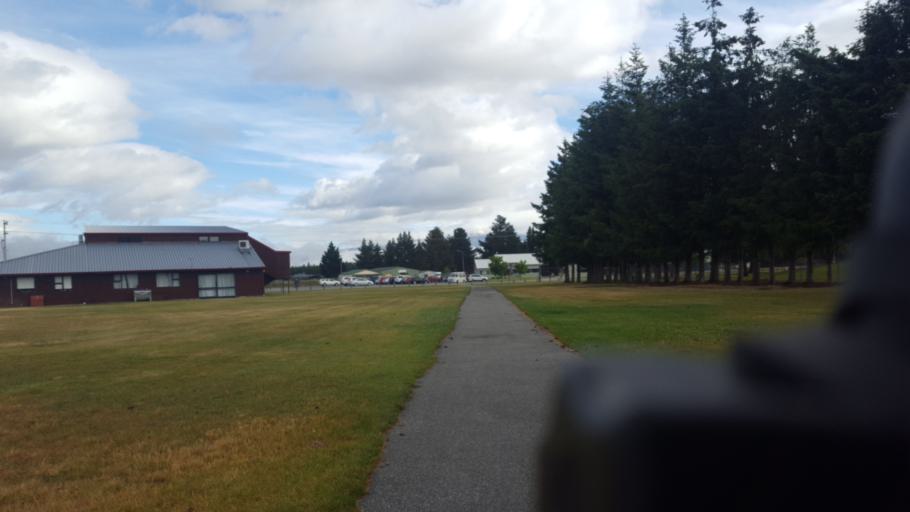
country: NZ
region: Otago
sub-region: Queenstown-Lakes District
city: Wanaka
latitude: -45.2440
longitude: 169.3820
